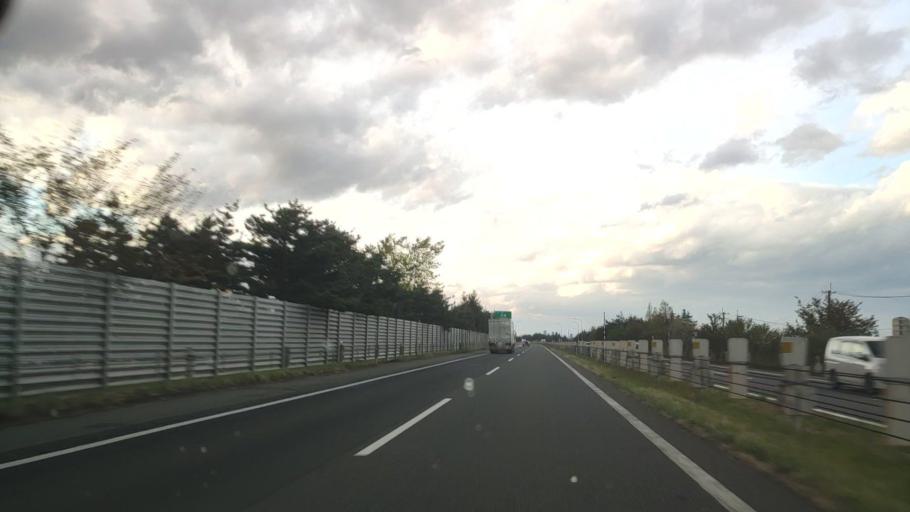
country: JP
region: Iwate
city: Hanamaki
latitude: 39.4397
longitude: 141.1080
